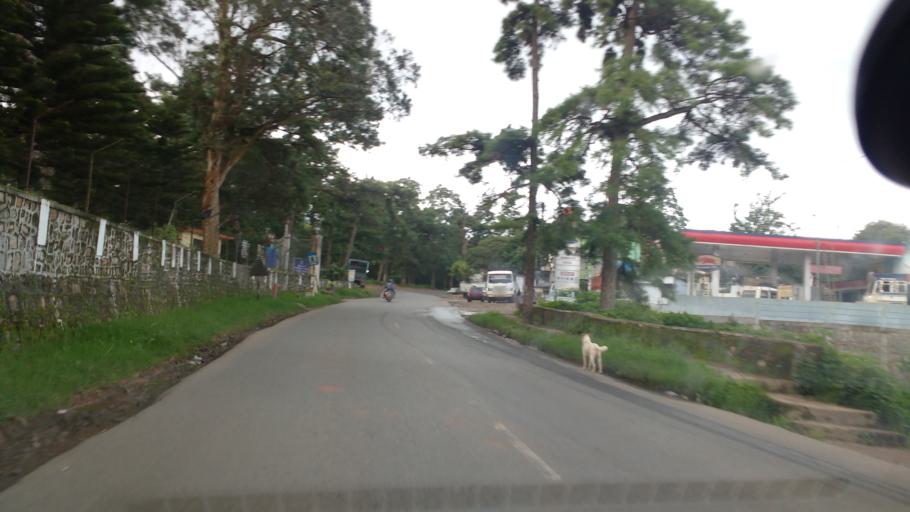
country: IN
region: Meghalaya
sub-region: East Khasi Hills
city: Shillong
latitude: 25.5664
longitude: 91.8552
